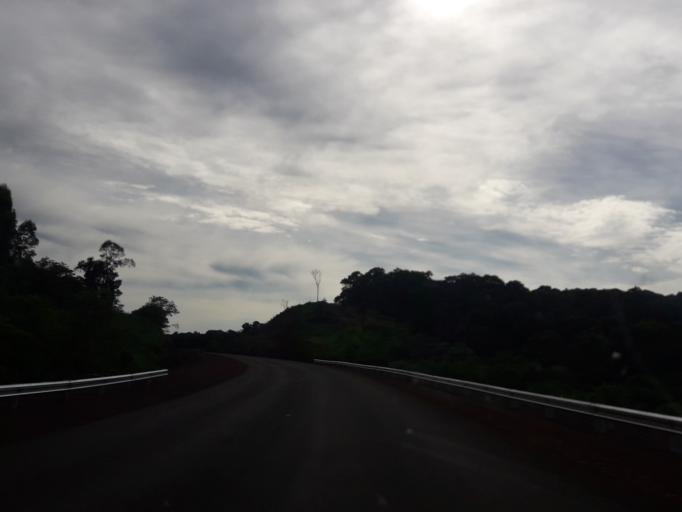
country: AR
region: Misiones
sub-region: Departamento de San Pedro
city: San Pedro
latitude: -26.5107
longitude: -53.9073
